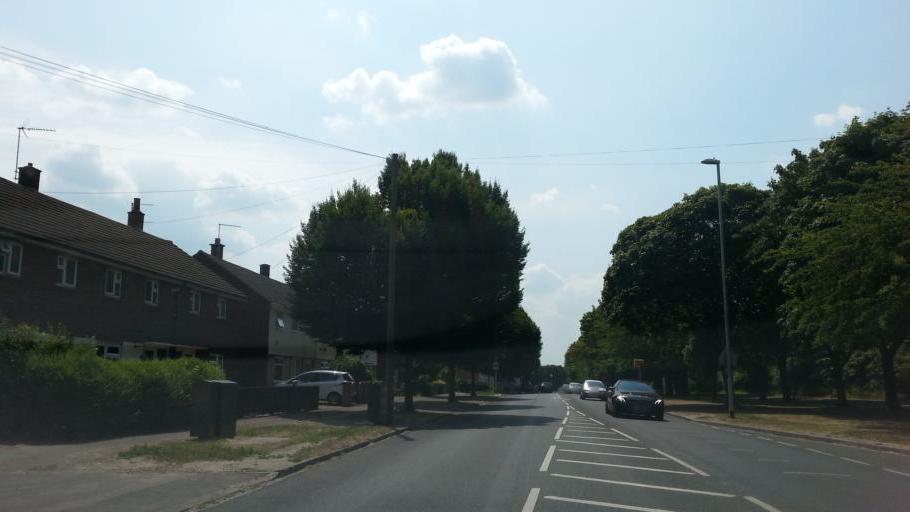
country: GB
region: England
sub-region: Cambridgeshire
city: Cambridge
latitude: 52.2095
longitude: 0.1632
